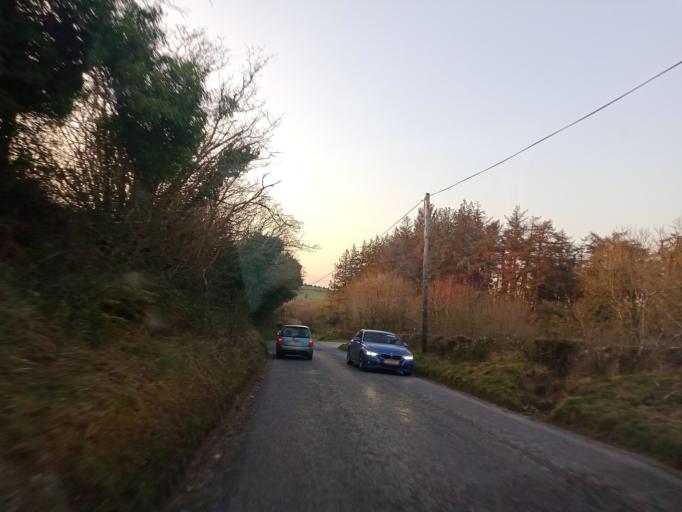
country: IE
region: Leinster
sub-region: Kilkenny
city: Castlecomer
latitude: 52.8595
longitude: -7.2674
